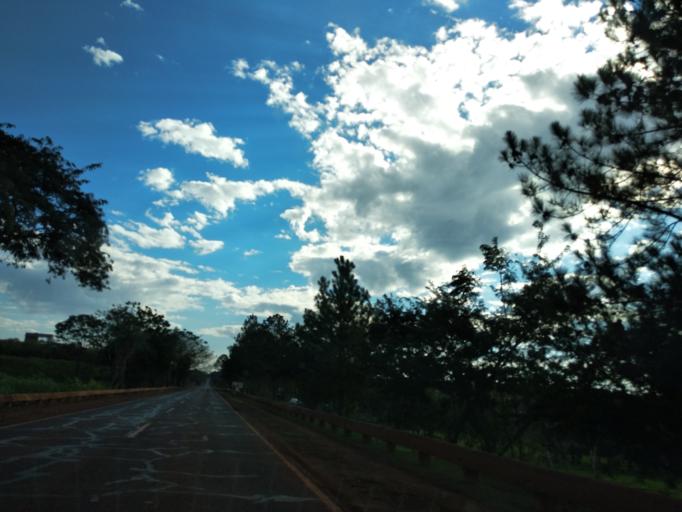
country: AR
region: Misiones
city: Jardin America
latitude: -27.0364
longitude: -55.2143
